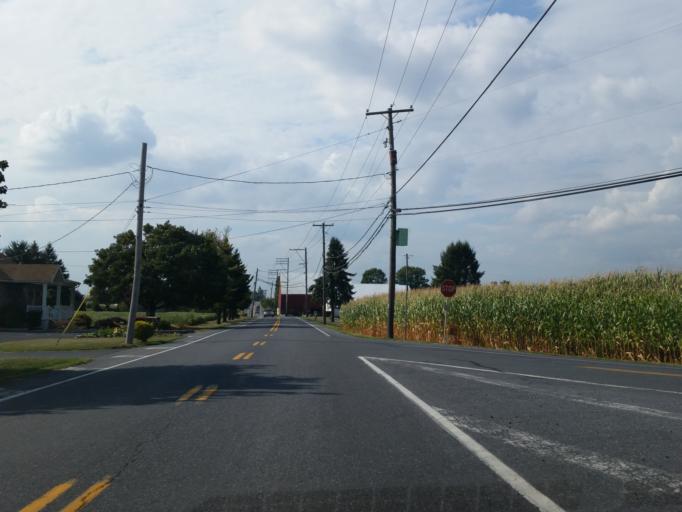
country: US
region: Pennsylvania
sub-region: Lancaster County
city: Manheim
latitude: 40.1751
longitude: -76.4569
